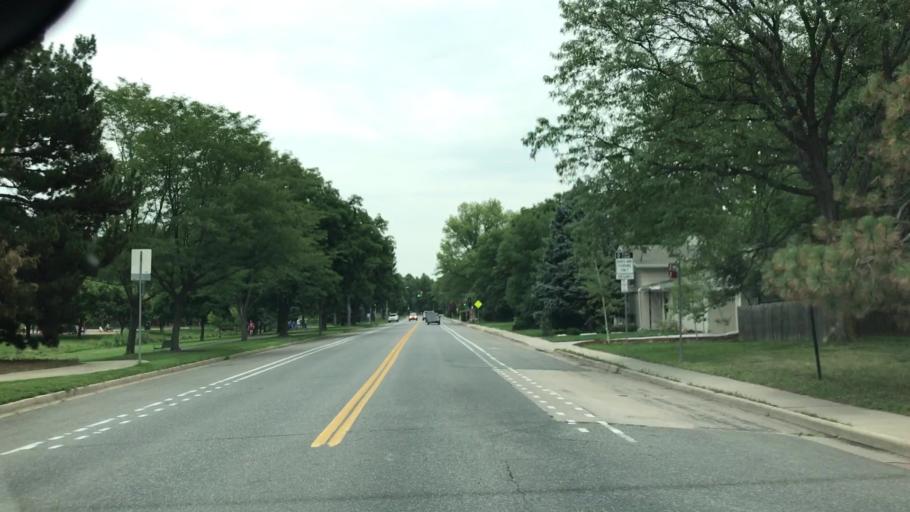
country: US
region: Colorado
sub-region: Arapahoe County
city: Cherry Hills Village
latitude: 39.6676
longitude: -104.9550
